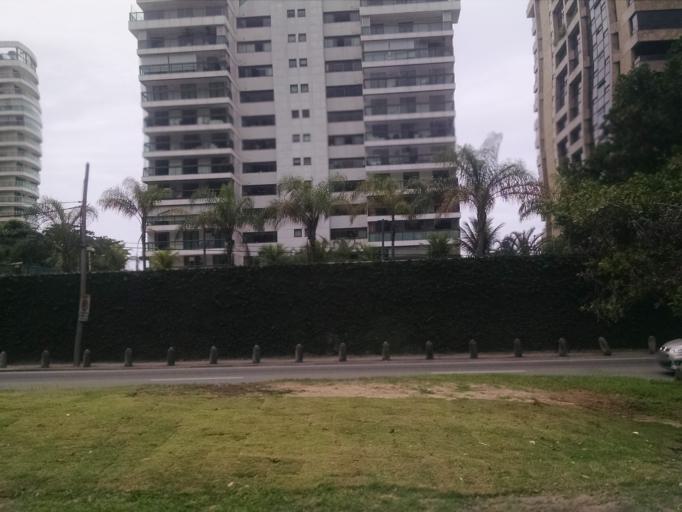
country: BR
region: Rio de Janeiro
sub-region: Rio De Janeiro
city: Rio de Janeiro
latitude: -22.9983
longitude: -43.2675
